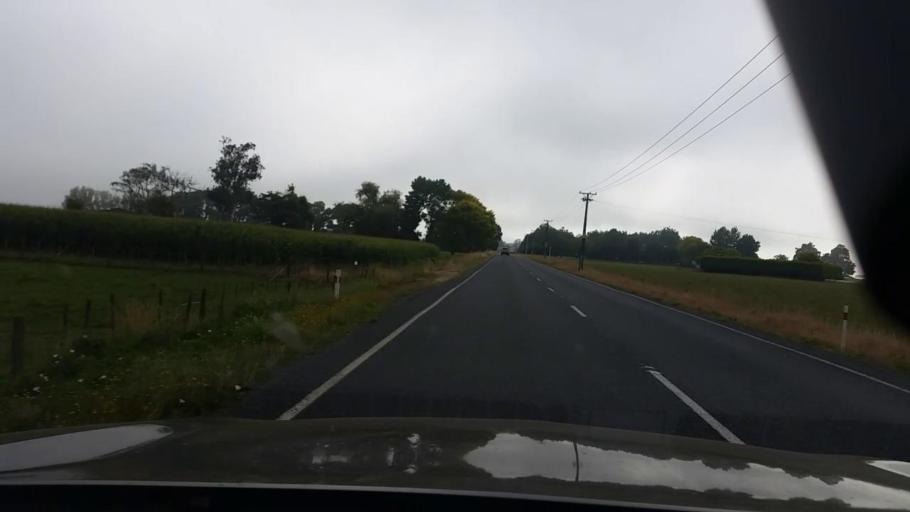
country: NZ
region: Waikato
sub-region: Hamilton City
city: Hamilton
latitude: -37.6254
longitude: 175.3233
